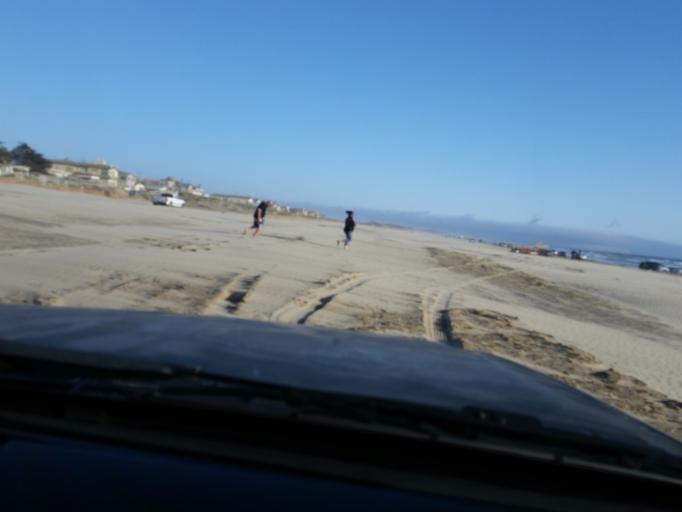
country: US
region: California
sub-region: San Luis Obispo County
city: Grover Beach
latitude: 35.1065
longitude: -120.6316
